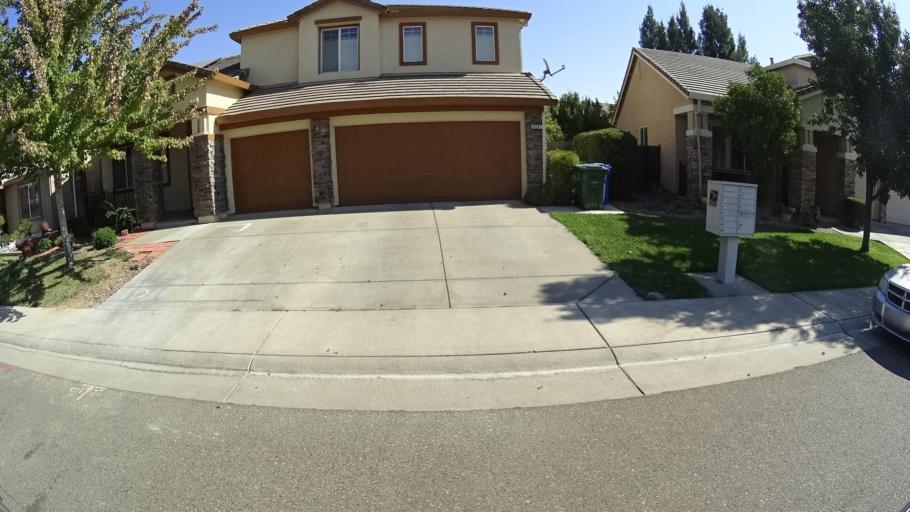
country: US
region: California
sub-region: Sacramento County
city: Laguna
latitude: 38.4461
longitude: -121.3945
